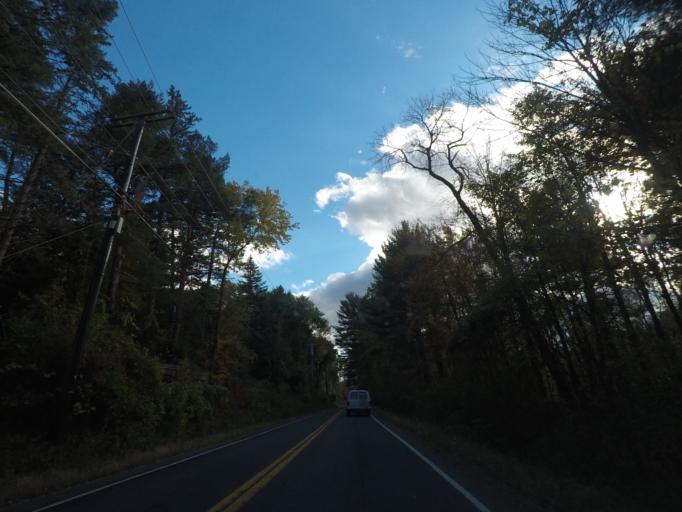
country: US
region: New York
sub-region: Schenectady County
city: Niskayuna
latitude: 42.7617
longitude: -73.8311
